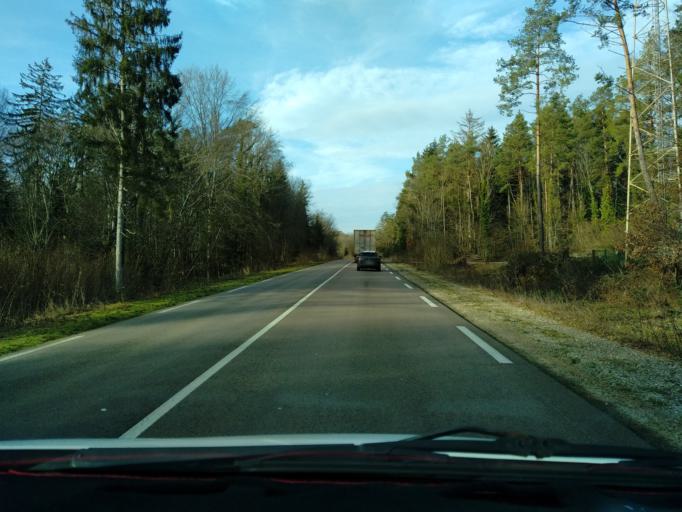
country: FR
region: Franche-Comte
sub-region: Departement de la Haute-Saone
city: Gray
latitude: 47.4024
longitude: 5.6415
